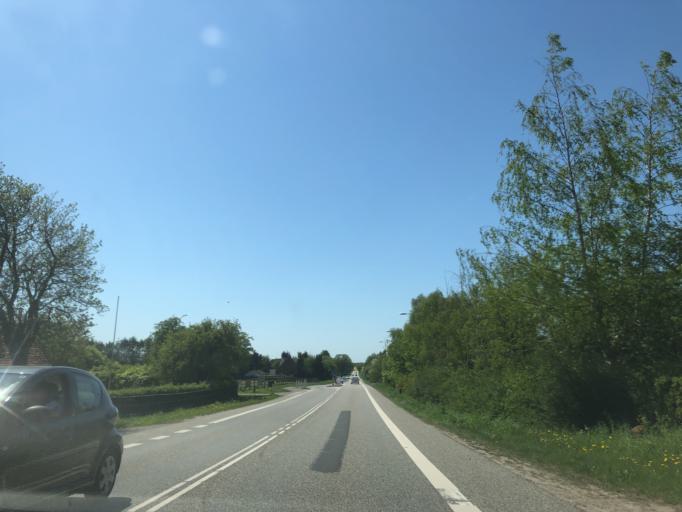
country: DK
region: Zealand
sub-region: Slagelse Kommune
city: Forlev
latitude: 55.3592
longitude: 11.2558
